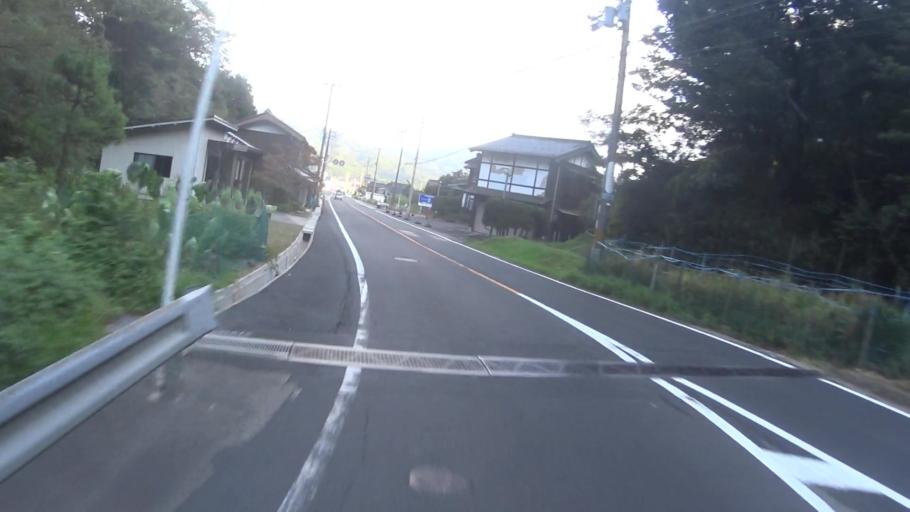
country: JP
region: Kyoto
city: Miyazu
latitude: 35.5405
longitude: 135.1107
